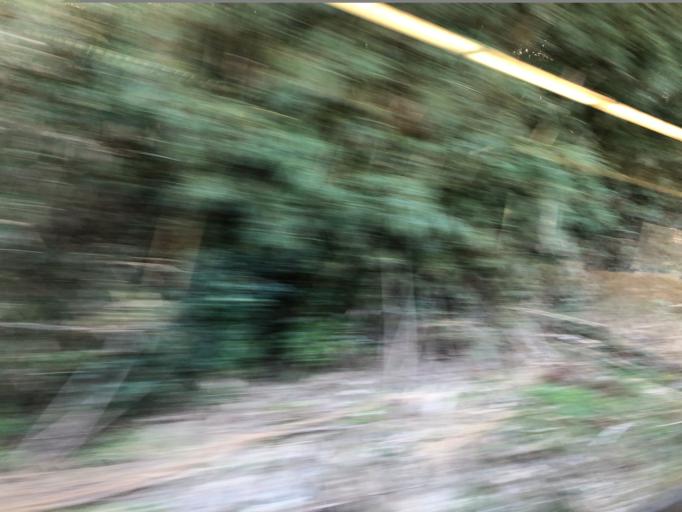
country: JP
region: Kochi
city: Nakamura
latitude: 33.0397
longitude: 133.0350
